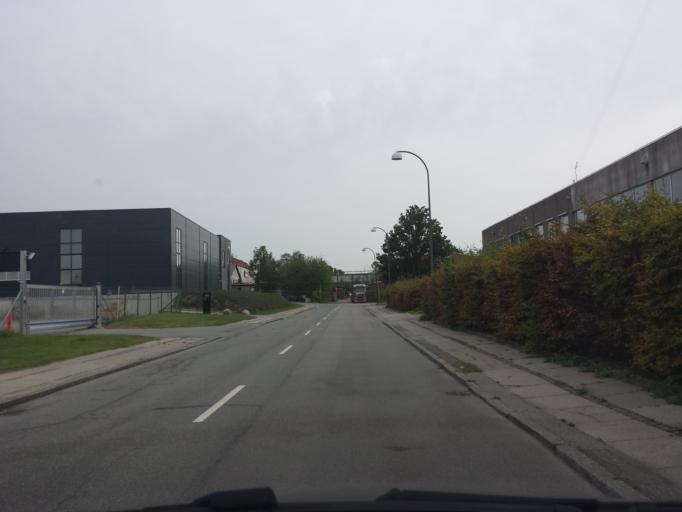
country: DK
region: Capital Region
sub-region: Herlev Kommune
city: Herlev
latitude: 55.7227
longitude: 12.4270
